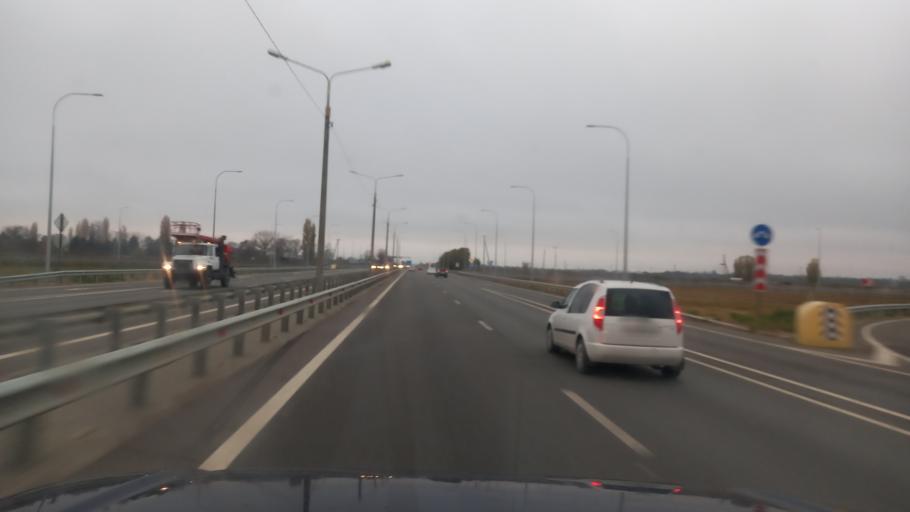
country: RU
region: Adygeya
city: Maykop
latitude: 44.6310
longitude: 40.0422
